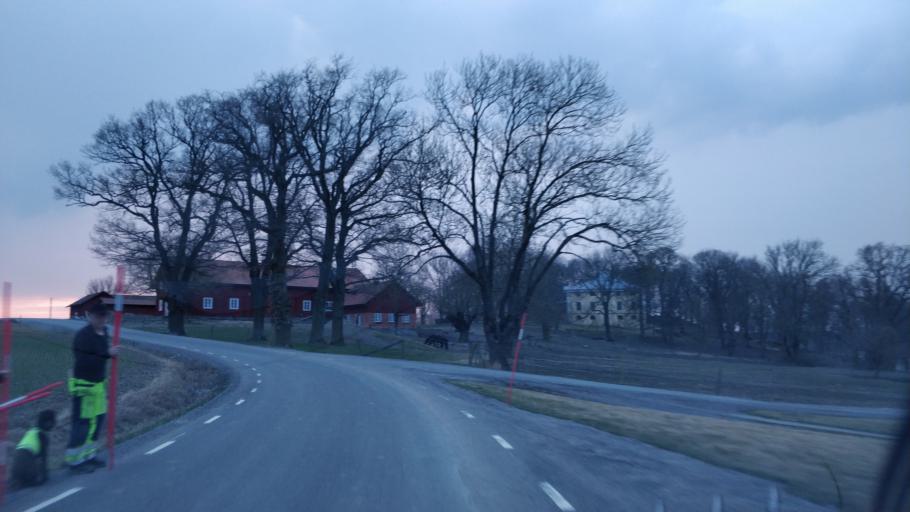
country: SE
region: Uppsala
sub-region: Enkopings Kommun
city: Orsundsbro
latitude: 59.7400
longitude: 17.1828
